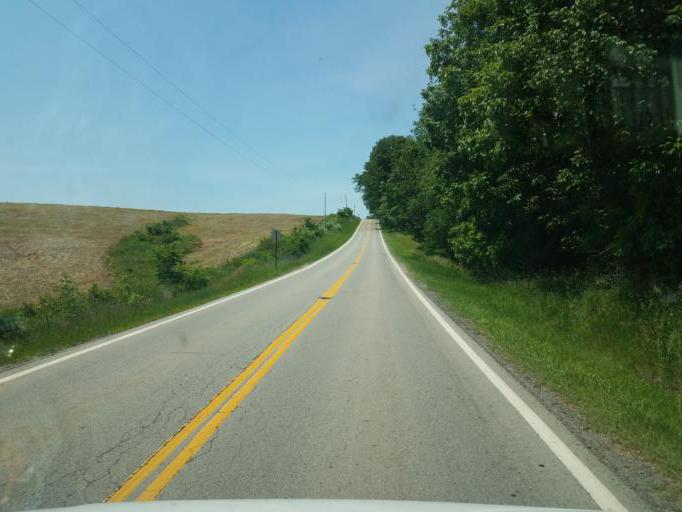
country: US
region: Ohio
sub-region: Ashland County
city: Loudonville
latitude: 40.7019
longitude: -82.2500
